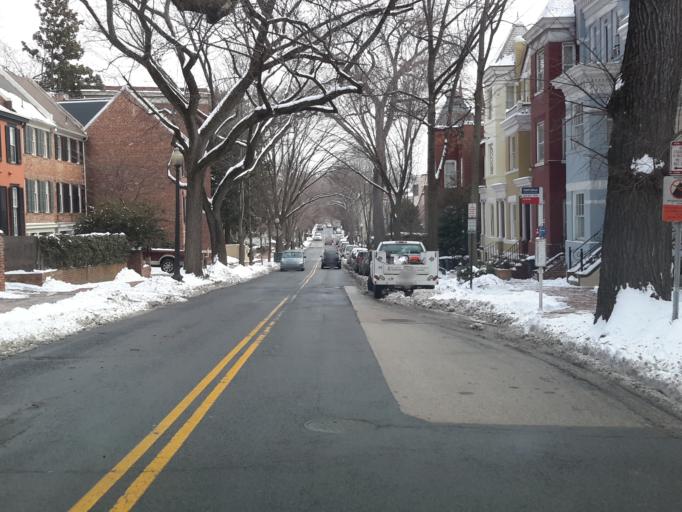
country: US
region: Washington, D.C.
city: Washington, D.C.
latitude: 38.9105
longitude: -77.0619
